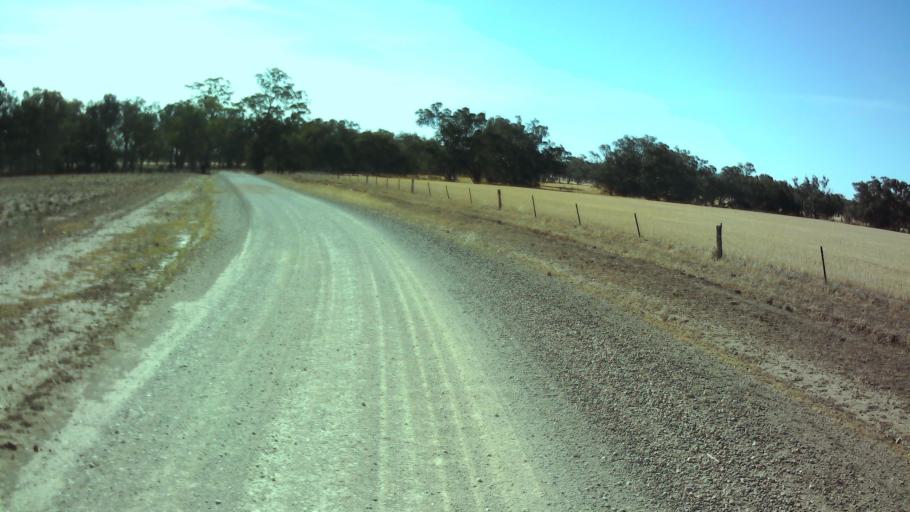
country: AU
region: New South Wales
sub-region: Weddin
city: Grenfell
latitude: -33.8381
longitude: 147.8771
